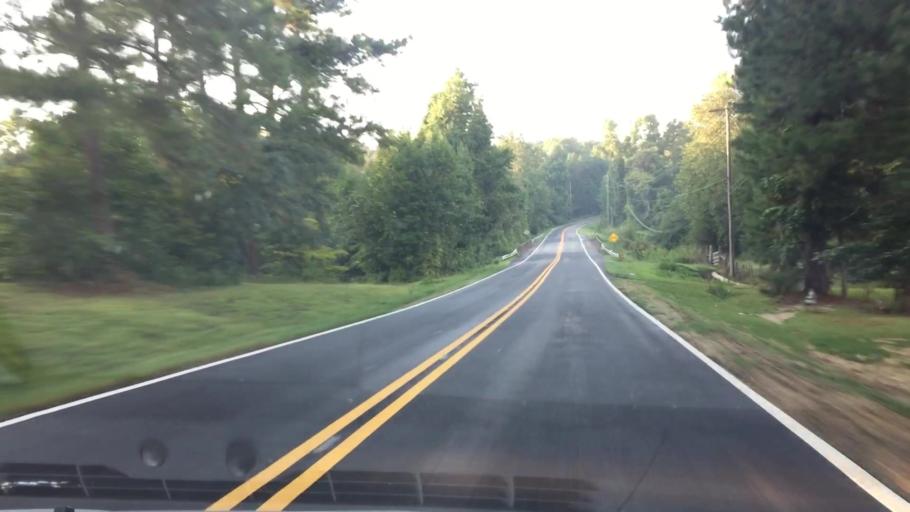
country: US
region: Georgia
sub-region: Henry County
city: McDonough
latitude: 33.4671
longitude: -84.1938
